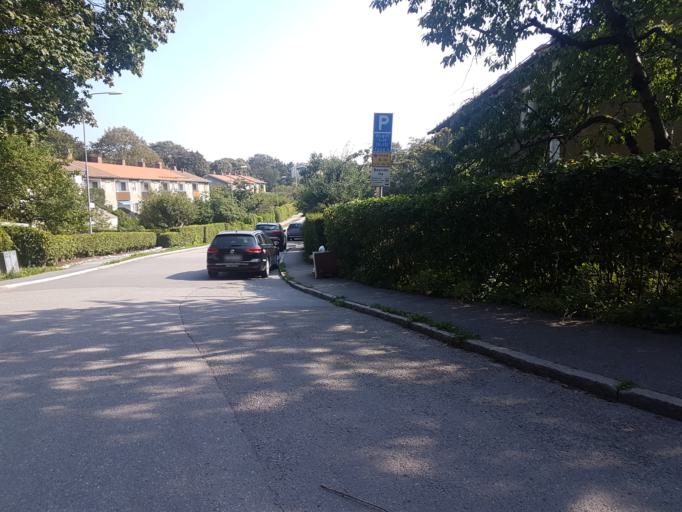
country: SE
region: Stockholm
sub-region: Stockholms Kommun
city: OEstermalm
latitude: 59.2950
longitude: 18.1114
